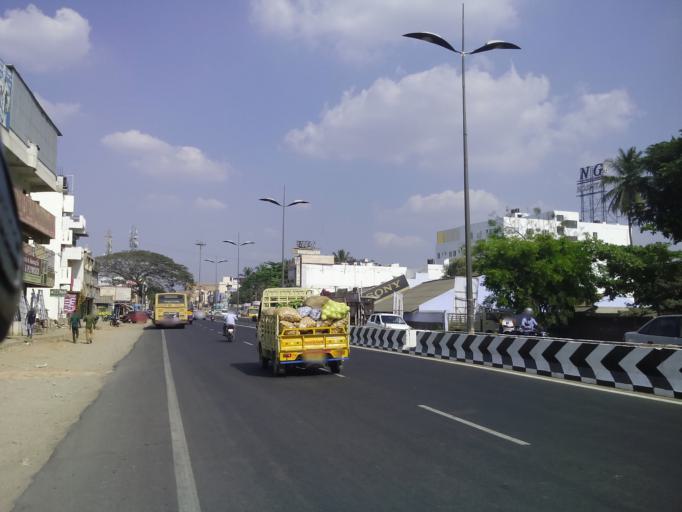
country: IN
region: Tamil Nadu
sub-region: Coimbatore
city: Singanallur
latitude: 11.0005
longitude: 77.0280
